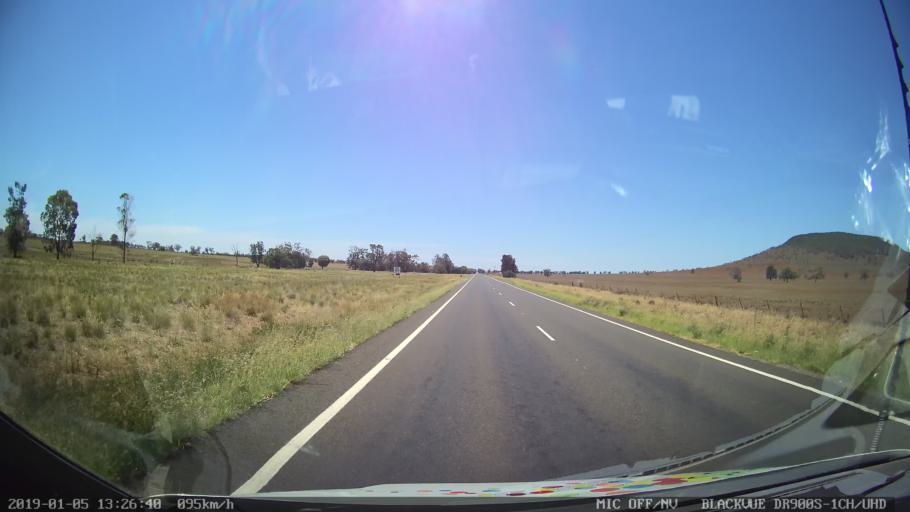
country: AU
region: New South Wales
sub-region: Gunnedah
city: Gunnedah
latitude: -31.0511
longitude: 150.0188
